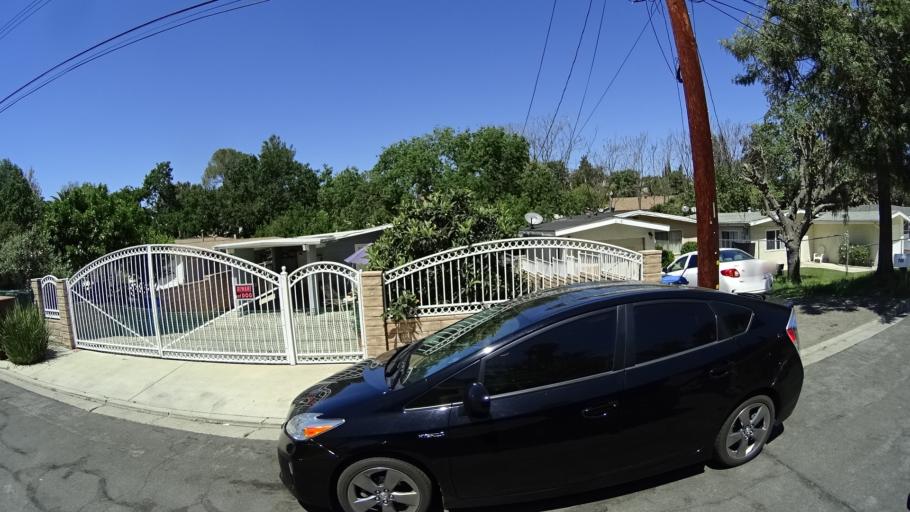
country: US
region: California
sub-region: Ventura County
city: Thousand Oaks
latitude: 34.1831
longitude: -118.8641
